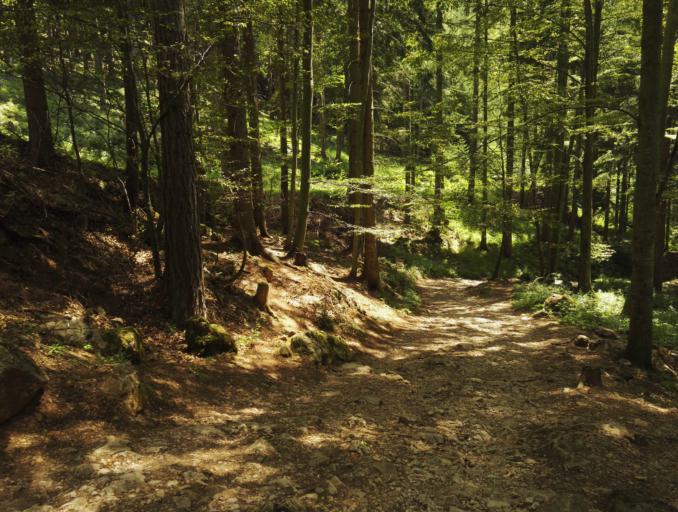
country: AT
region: Styria
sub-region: Politischer Bezirk Graz-Umgebung
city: Rothelstein
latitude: 47.3477
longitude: 15.3968
